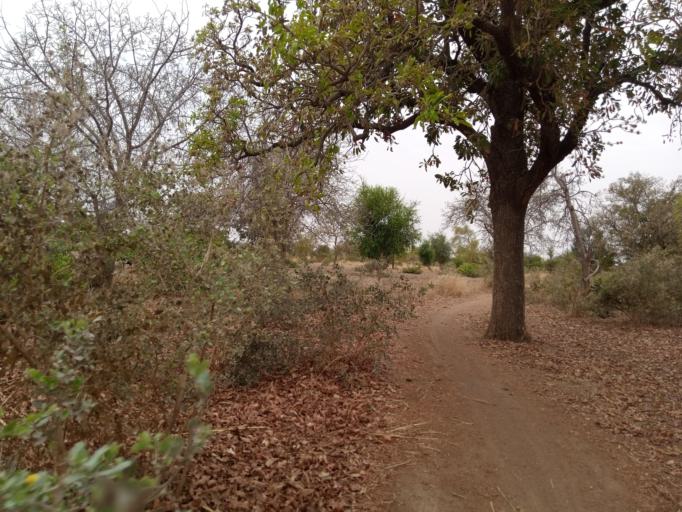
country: BF
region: Boucle du Mouhoun
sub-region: Province de la Kossi
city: Nouna
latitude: 12.8430
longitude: -4.0771
